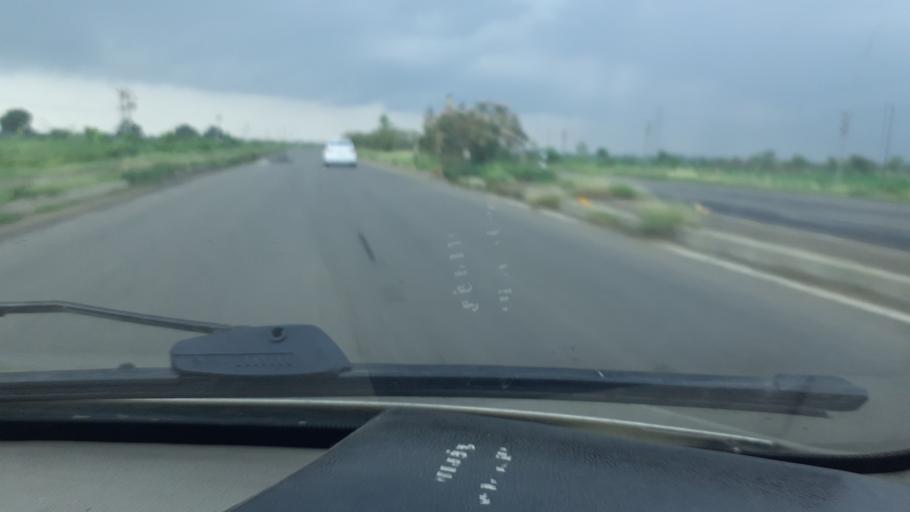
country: IN
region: Tamil Nadu
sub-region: Thoothukkudi
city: Kovilpatti
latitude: 9.1129
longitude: 77.8121
